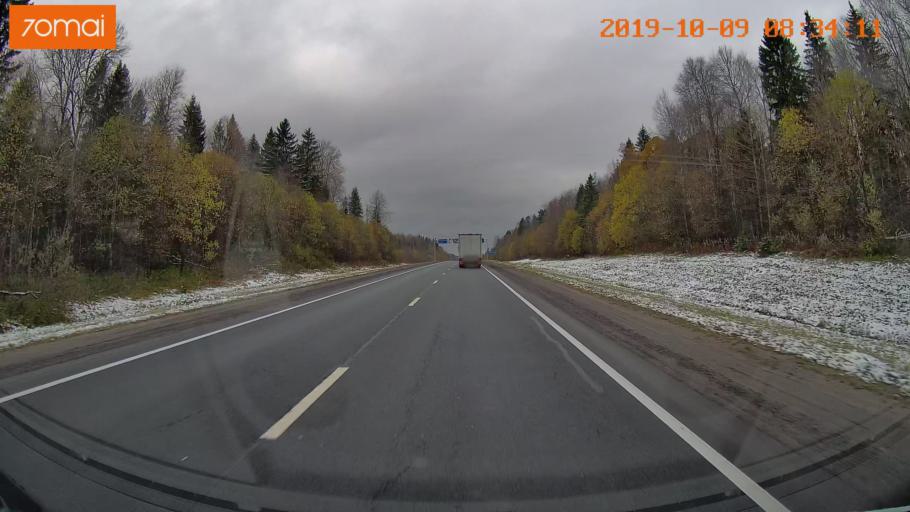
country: RU
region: Vologda
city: Gryazovets
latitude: 58.8933
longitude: 40.1872
